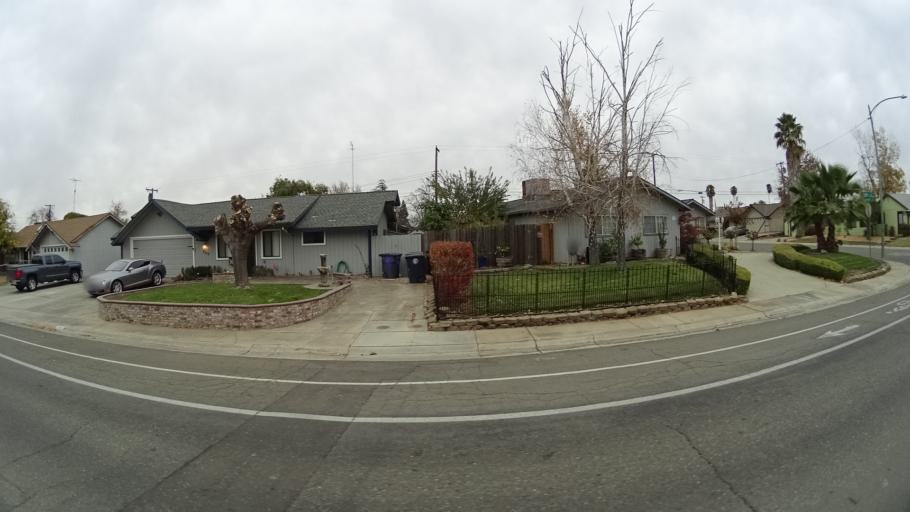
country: US
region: California
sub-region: Sacramento County
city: Citrus Heights
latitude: 38.6971
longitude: -121.2965
